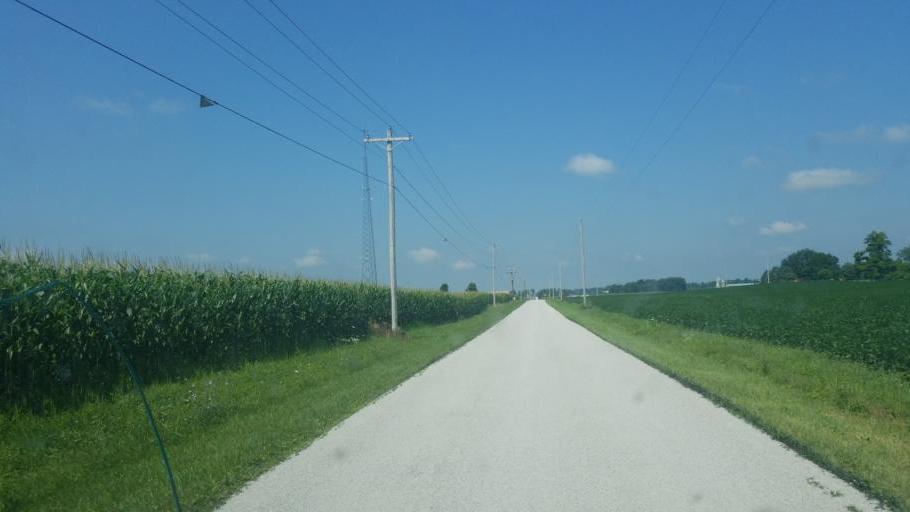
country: US
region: Ohio
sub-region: Hardin County
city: Kenton
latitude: 40.7037
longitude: -83.7072
